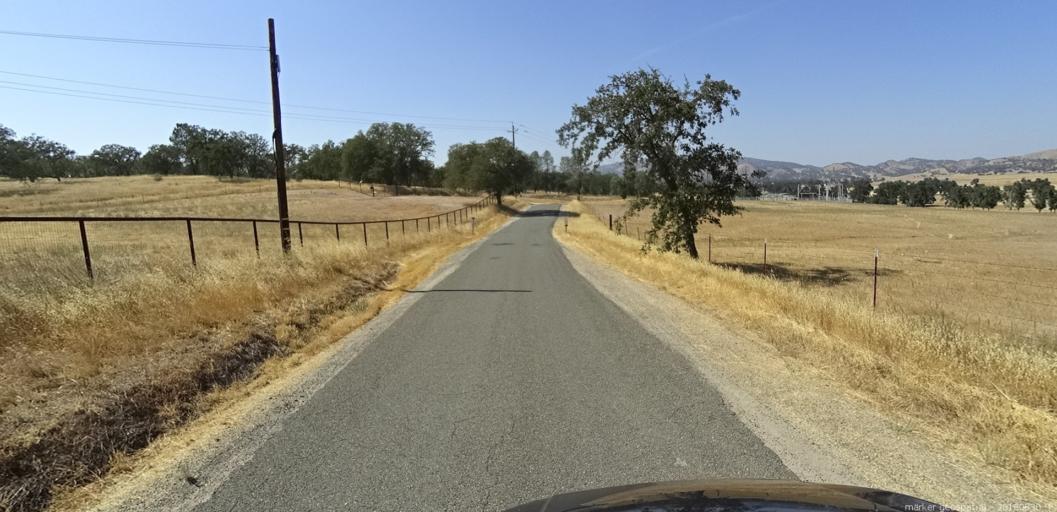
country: US
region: California
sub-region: Monterey County
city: King City
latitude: 36.0106
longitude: -121.1669
